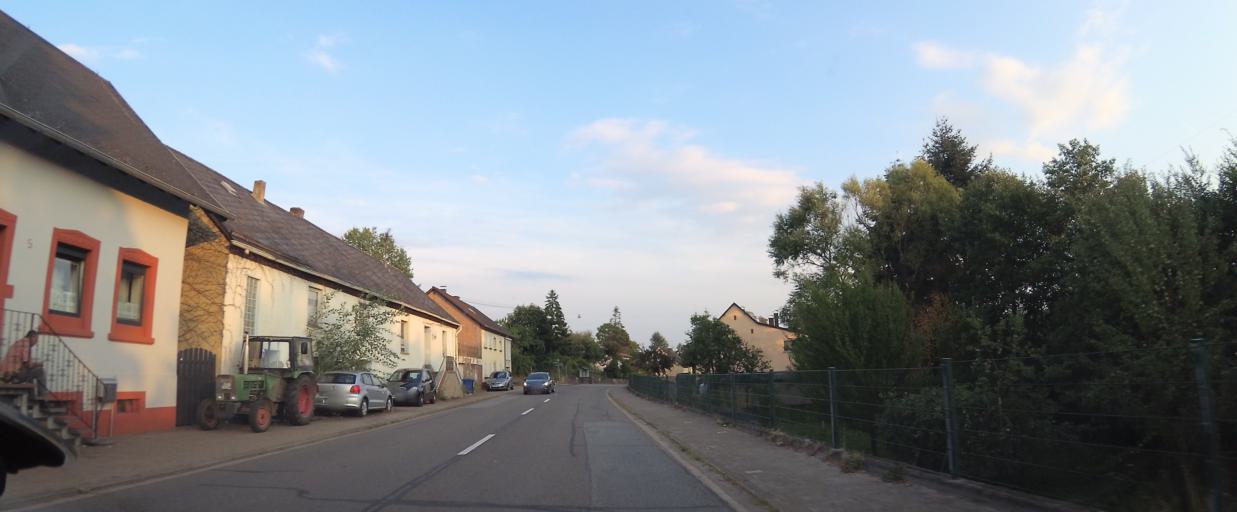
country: DE
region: Saarland
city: Wadern
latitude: 49.5788
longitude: 6.8949
